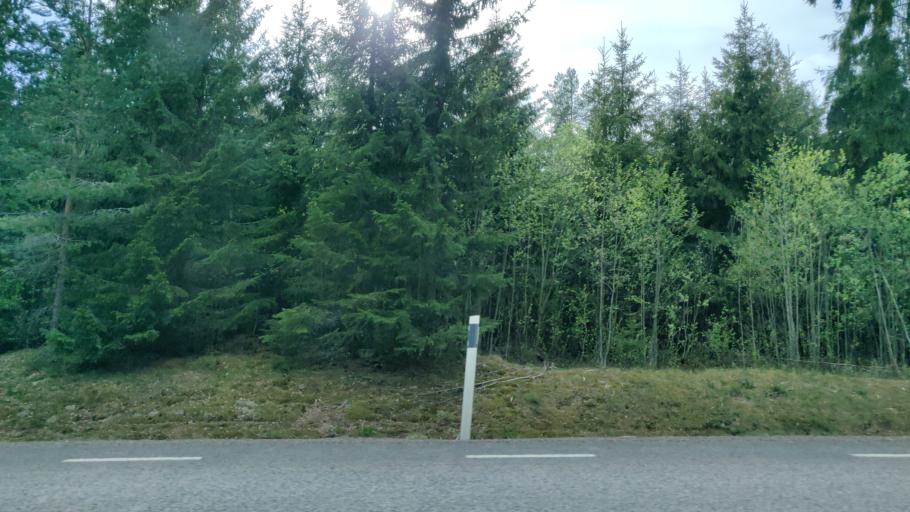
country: SE
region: Vaermland
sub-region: Forshaga Kommun
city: Deje
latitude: 59.5849
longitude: 13.4607
